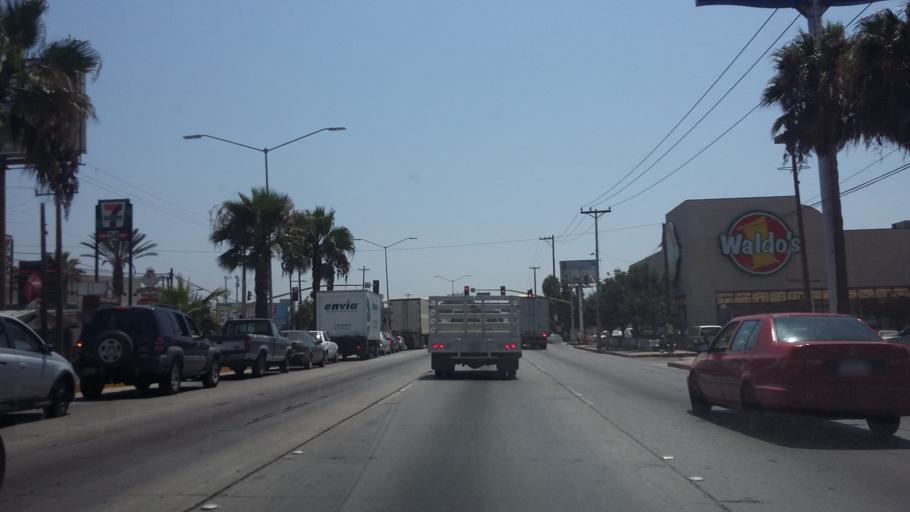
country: MX
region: Baja California
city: Ensenada
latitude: 31.8265
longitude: -116.6000
